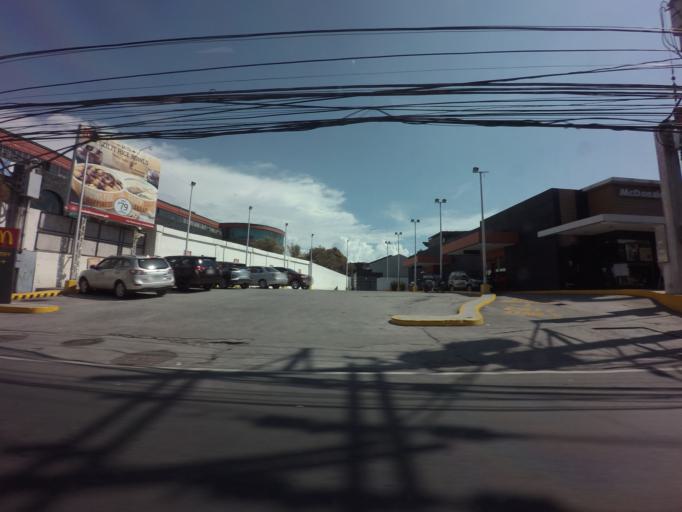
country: PH
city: Sambayanihan People's Village
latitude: 14.4414
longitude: 120.9984
